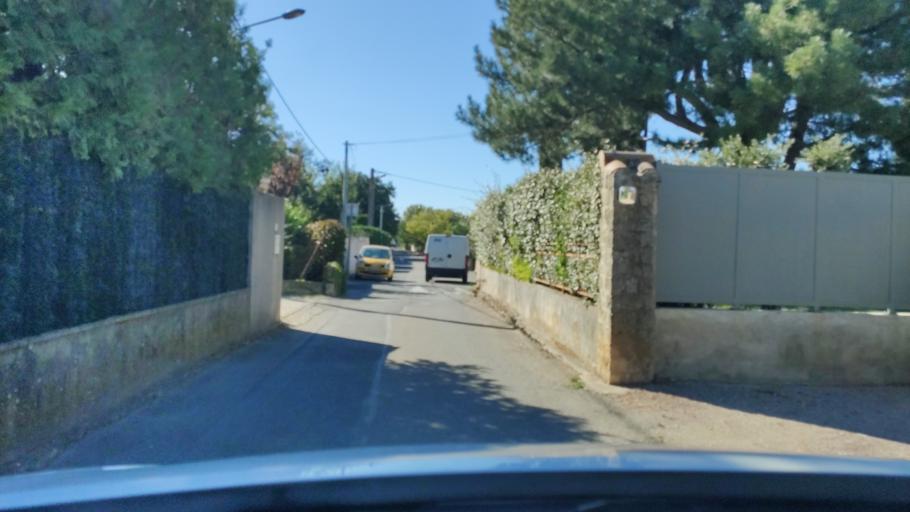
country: FR
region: Provence-Alpes-Cote d'Azur
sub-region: Departement du Vaucluse
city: Morieres-les-Avignon
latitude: 43.9435
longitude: 4.9016
